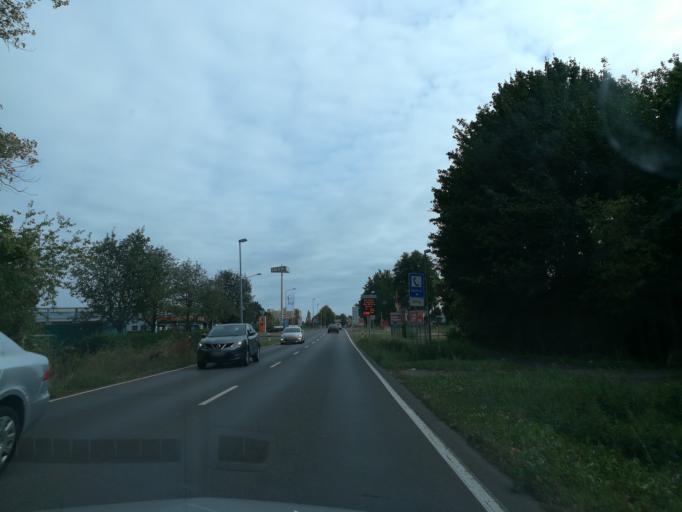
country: DE
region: Saxony-Anhalt
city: Neue Neustadt
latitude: 52.1684
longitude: 11.6047
